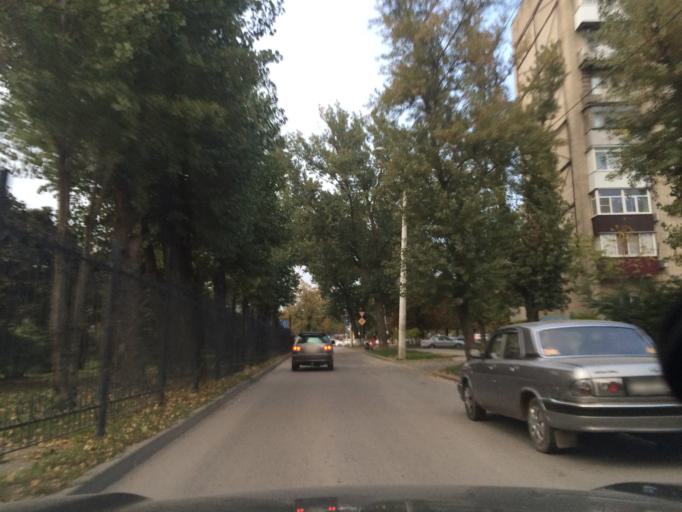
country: RU
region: Rostov
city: Rostov-na-Donu
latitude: 47.2070
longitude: 39.6338
